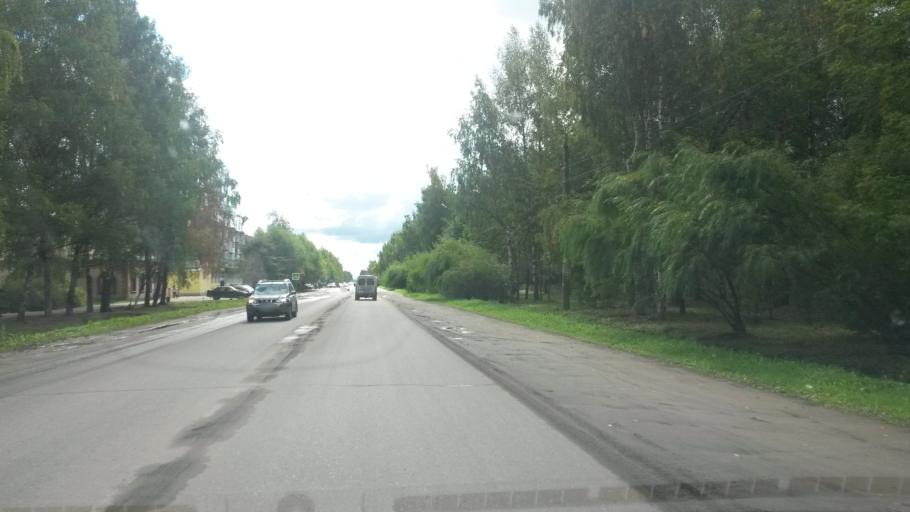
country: RU
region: Ivanovo
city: Zavolzhsk
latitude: 57.4893
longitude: 42.1399
